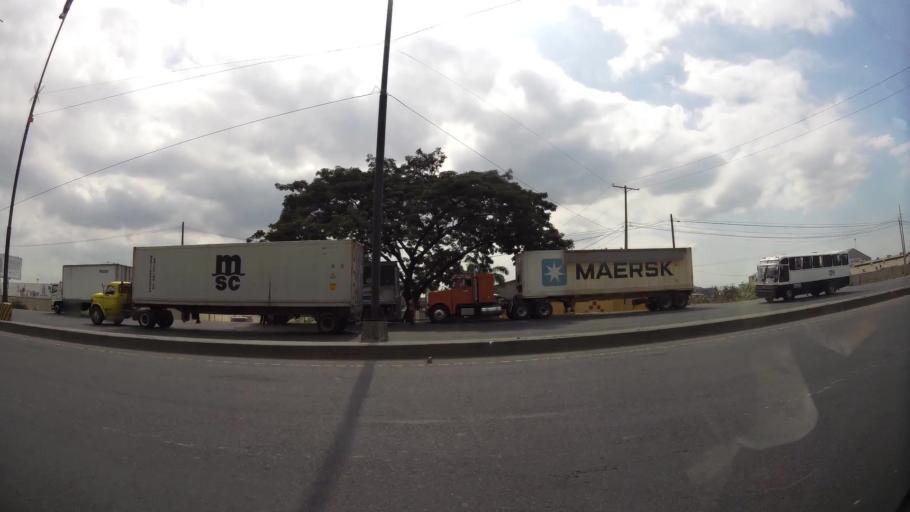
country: EC
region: Guayas
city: Santa Lucia
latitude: -2.0858
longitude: -79.9456
